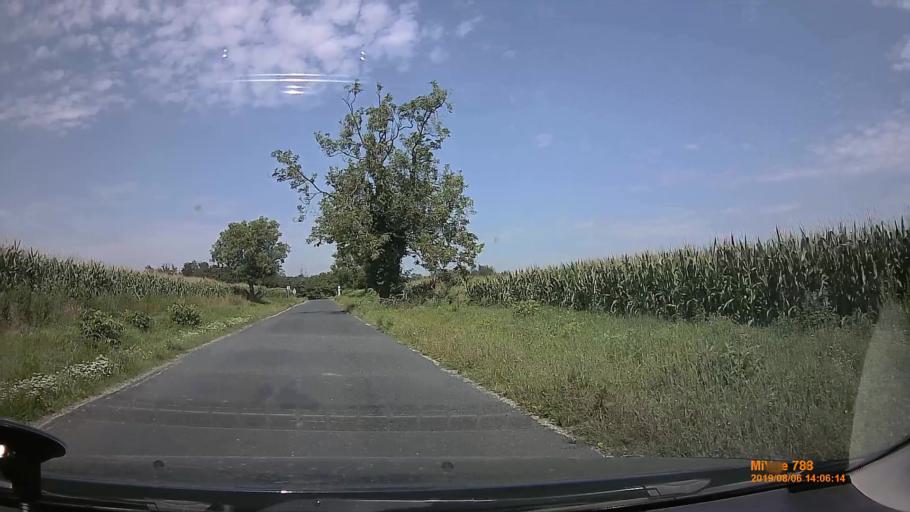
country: HU
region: Zala
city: Zalakomar
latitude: 46.5195
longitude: 17.0861
